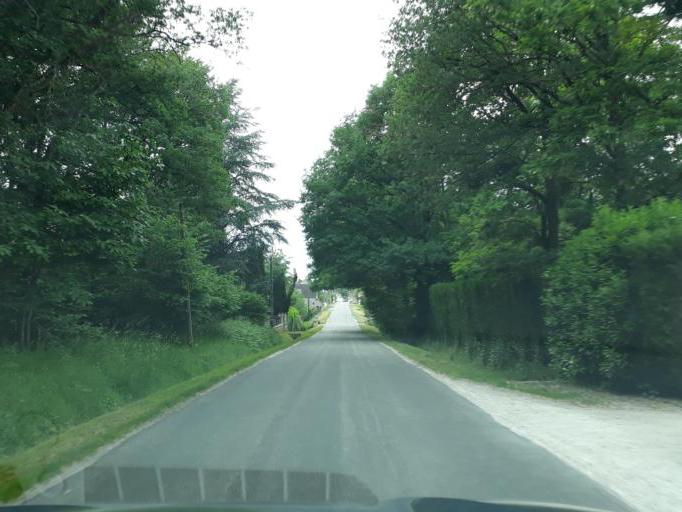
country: FR
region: Centre
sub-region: Departement du Loiret
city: Saint-Pere-sur-Loire
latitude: 47.7270
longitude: 2.3090
